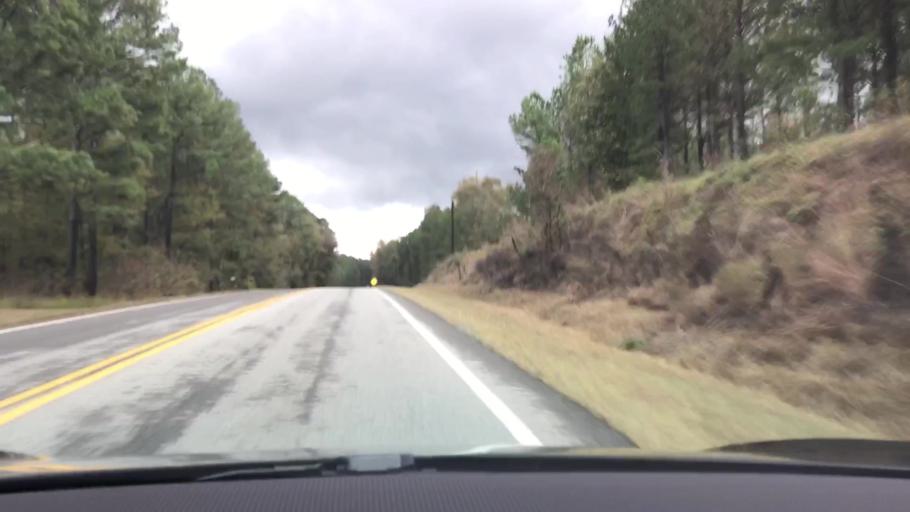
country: US
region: Georgia
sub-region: Greene County
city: Greensboro
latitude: 33.7051
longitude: -83.2875
